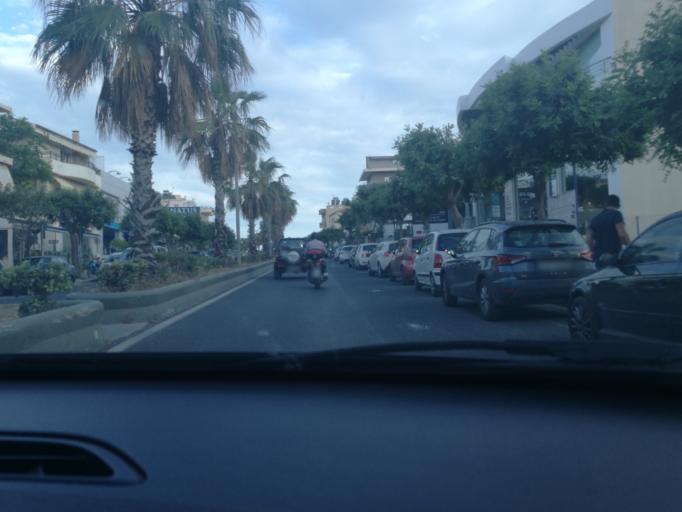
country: GR
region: Crete
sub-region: Nomos Irakleiou
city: Irakleion
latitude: 35.3182
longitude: 25.1449
